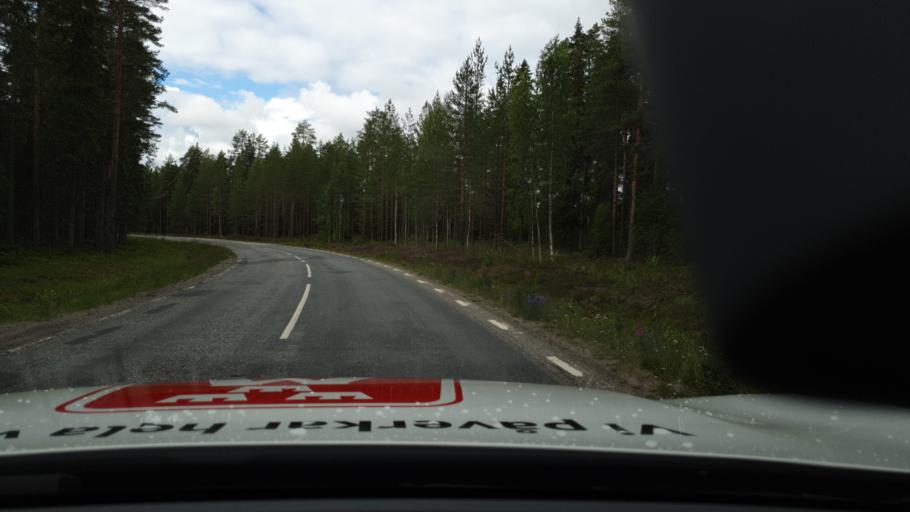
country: SE
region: Norrbotten
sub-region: Bodens Kommun
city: Saevast
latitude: 65.6044
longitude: 21.7468
